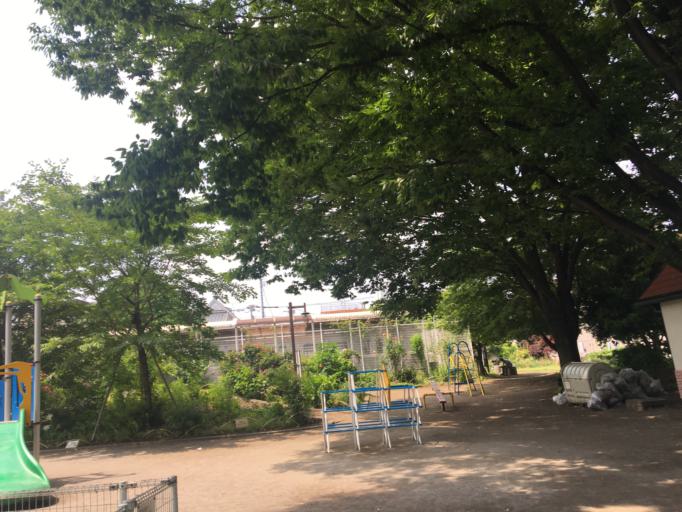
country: JP
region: Tokyo
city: Tokyo
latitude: 35.7312
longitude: 139.6936
